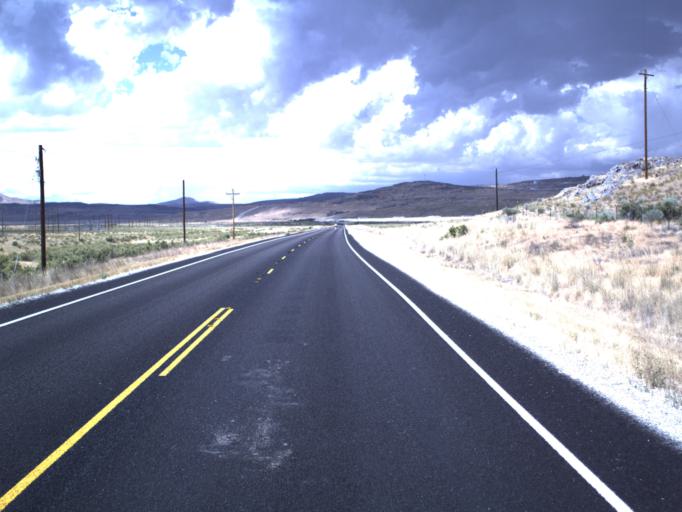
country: US
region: Utah
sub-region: Box Elder County
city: Tremonton
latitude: 41.6163
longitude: -112.3799
